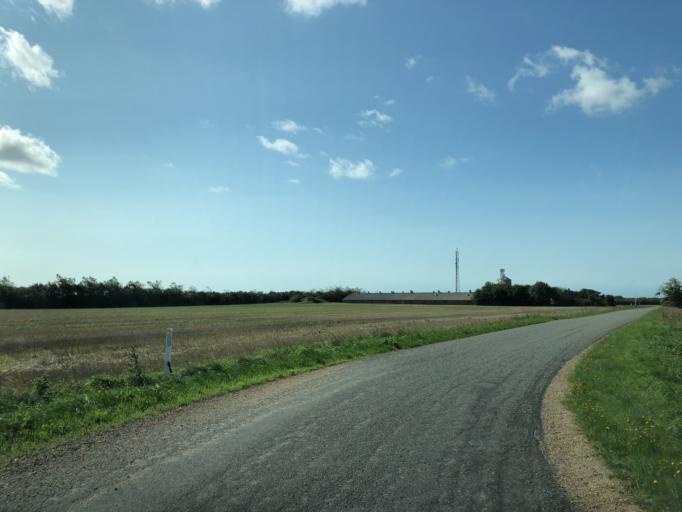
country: DK
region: Central Jutland
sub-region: Holstebro Kommune
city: Ulfborg
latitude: 56.2618
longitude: 8.1756
